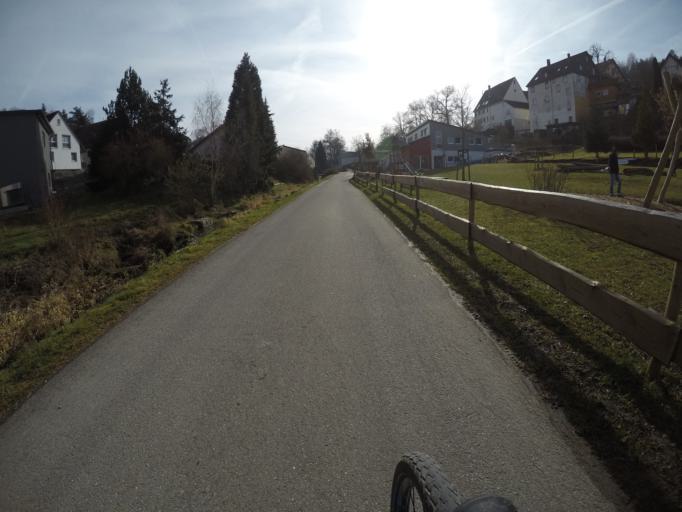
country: DE
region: Baden-Wuerttemberg
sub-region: Karlsruhe Region
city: Wildberg
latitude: 48.6184
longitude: 8.7786
